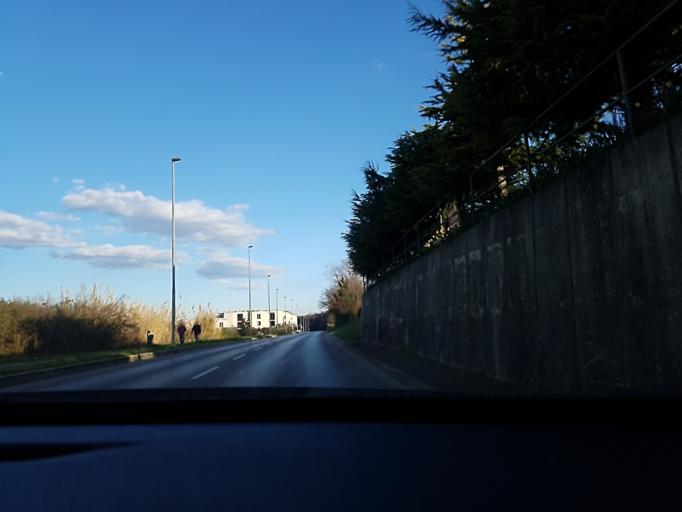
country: SI
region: Koper-Capodistria
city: Koper
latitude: 45.5424
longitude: 13.6966
